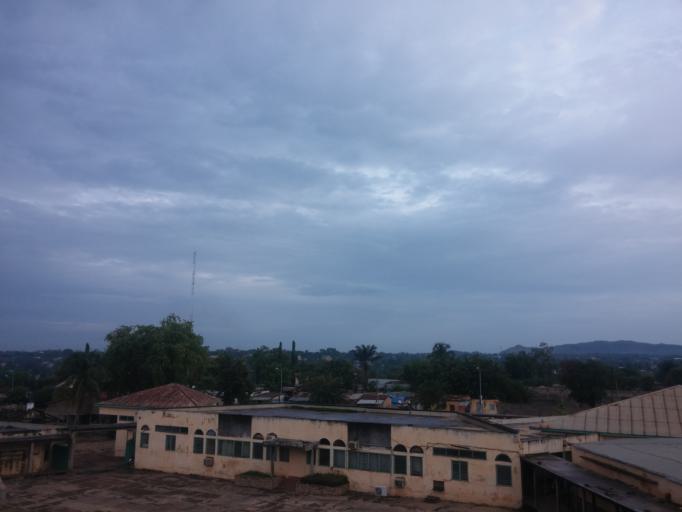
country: TG
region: Kara
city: Kara
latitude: 9.5502
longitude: 1.2023
